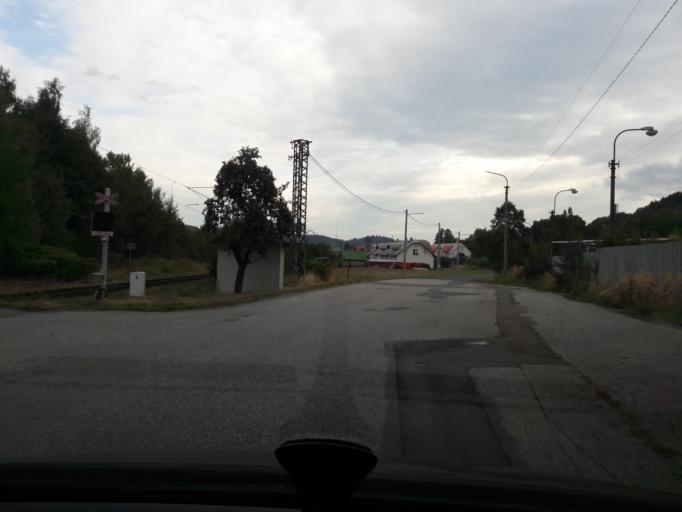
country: CZ
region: Olomoucky
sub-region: Okres Sumperk
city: Loucna nad Desnou
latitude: 50.0661
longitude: 17.0883
